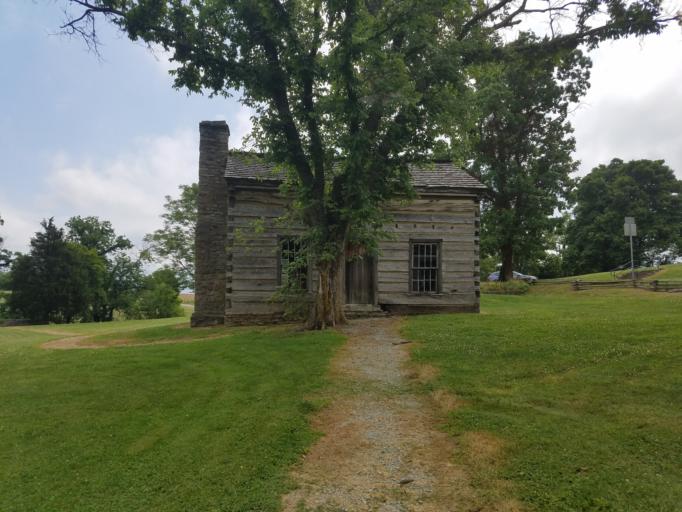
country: US
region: Kentucky
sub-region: Washington County
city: Springfield
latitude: 37.7603
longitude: -85.2146
